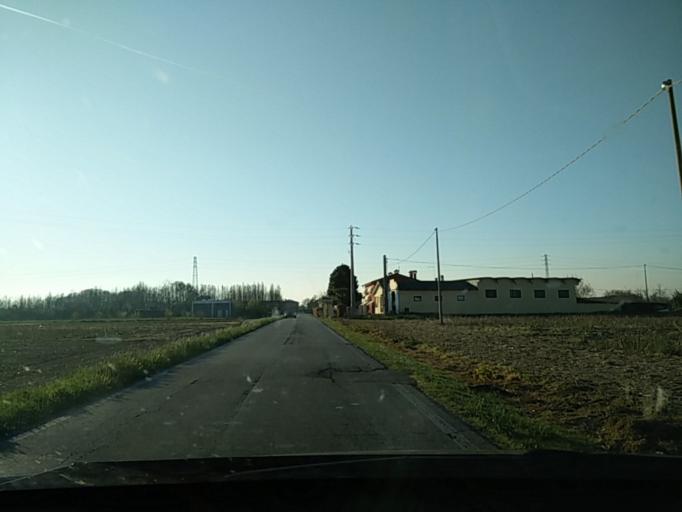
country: IT
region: Veneto
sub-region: Provincia di Venezia
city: Passarella
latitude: 45.6069
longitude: 12.5805
